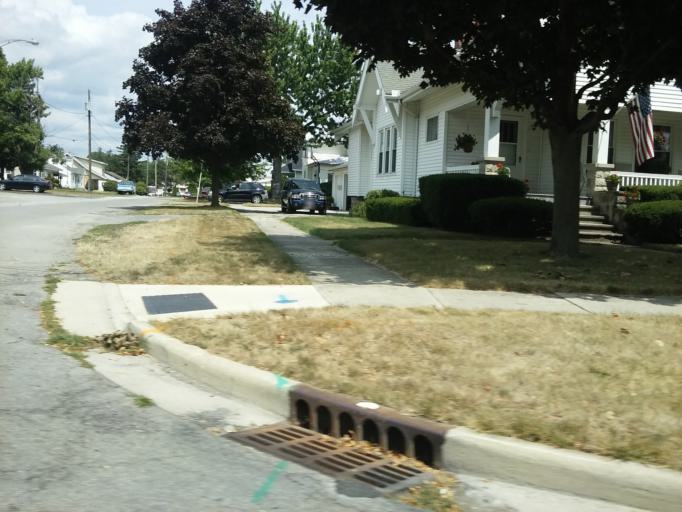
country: US
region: Ohio
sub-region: Hancock County
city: Findlay
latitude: 41.0407
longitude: -83.6644
